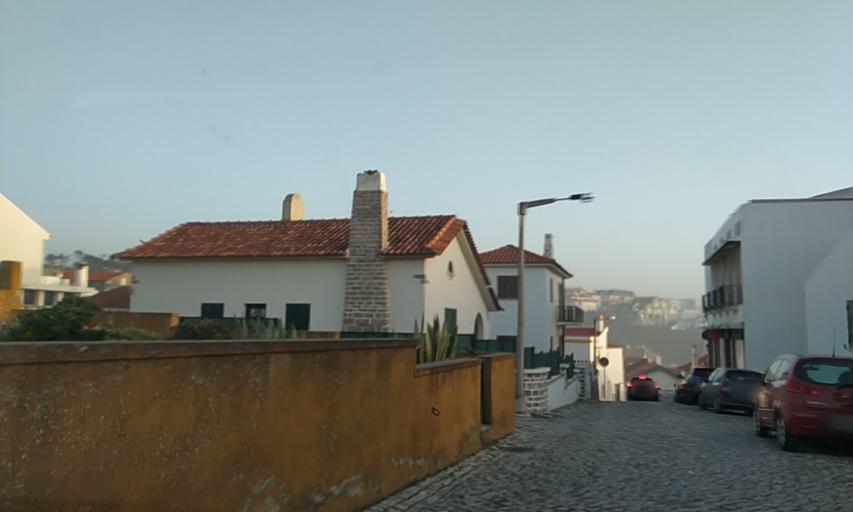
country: PT
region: Leiria
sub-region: Alcobaca
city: Pataias
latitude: 39.7575
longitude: -9.0321
